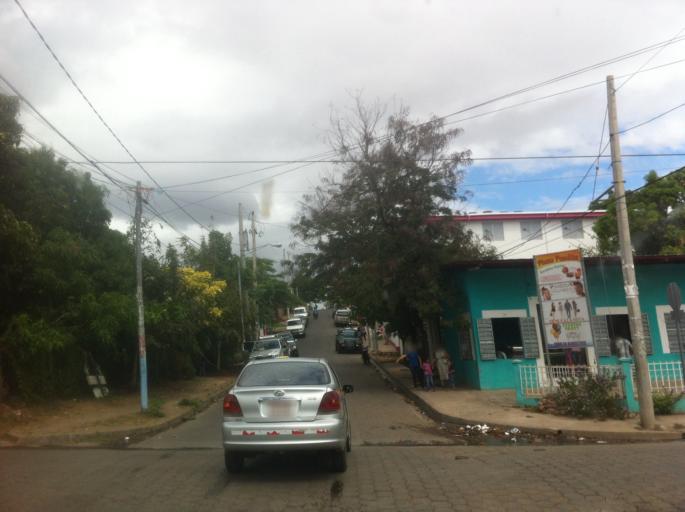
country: NI
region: Chontales
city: Juigalpa
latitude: 12.1000
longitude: -85.3624
